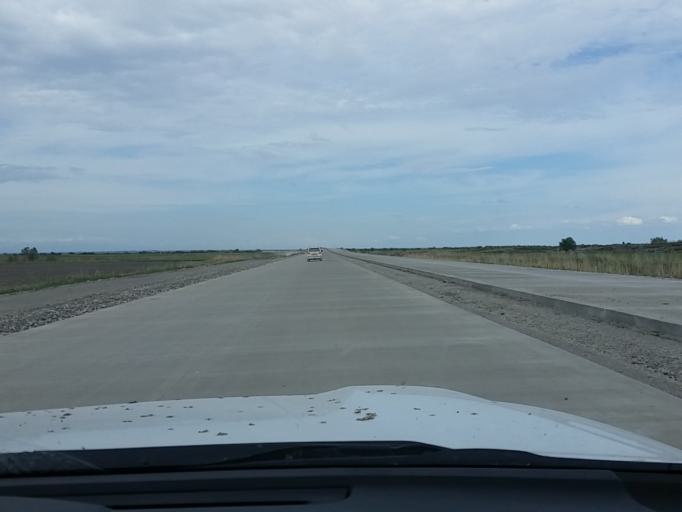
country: KZ
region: Almaty Oblysy
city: Zharkent
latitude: 44.0302
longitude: 79.9197
